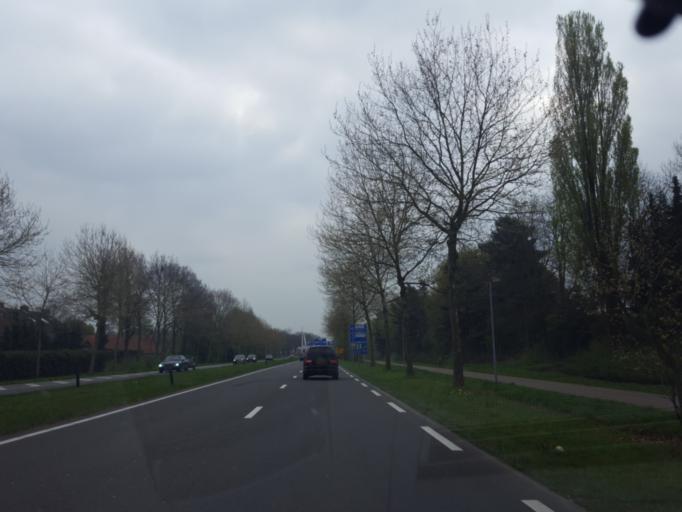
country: NL
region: Limburg
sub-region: Gemeente Weert
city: Weert
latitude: 51.2630
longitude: 5.6935
